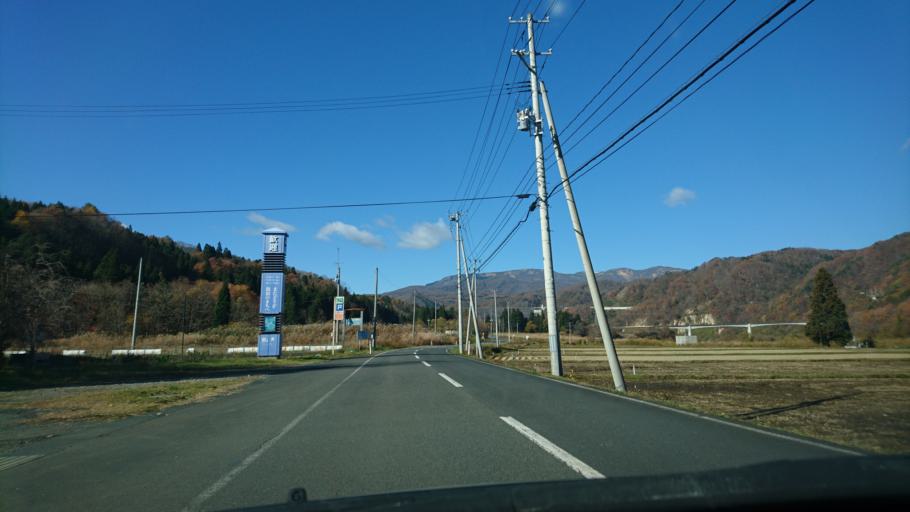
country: JP
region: Iwate
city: Mizusawa
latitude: 39.1169
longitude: 140.9430
